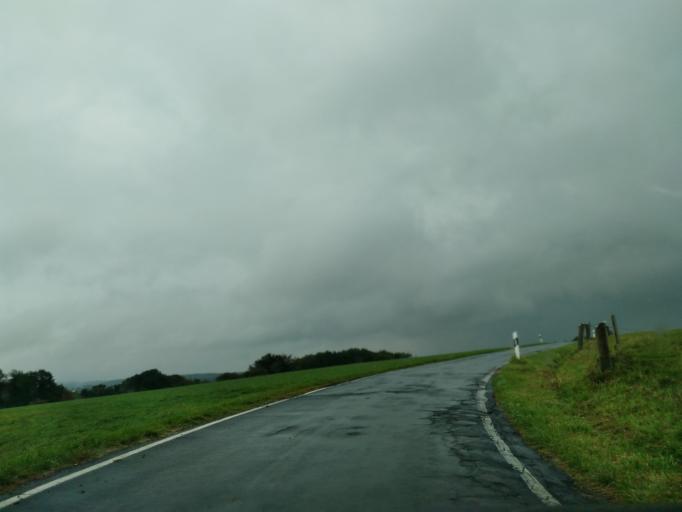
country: DE
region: Rheinland-Pfalz
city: Asbach
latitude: 50.6704
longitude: 7.4354
